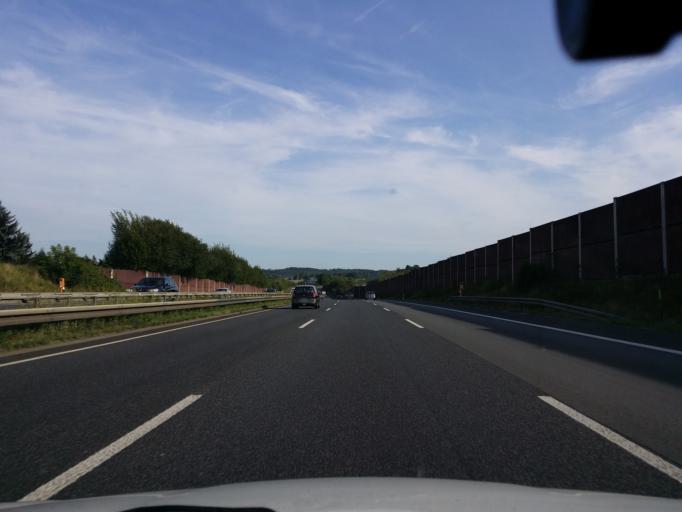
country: DE
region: North Rhine-Westphalia
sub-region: Regierungsbezirk Koln
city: Bad Honnef
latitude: 50.7053
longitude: 7.2512
